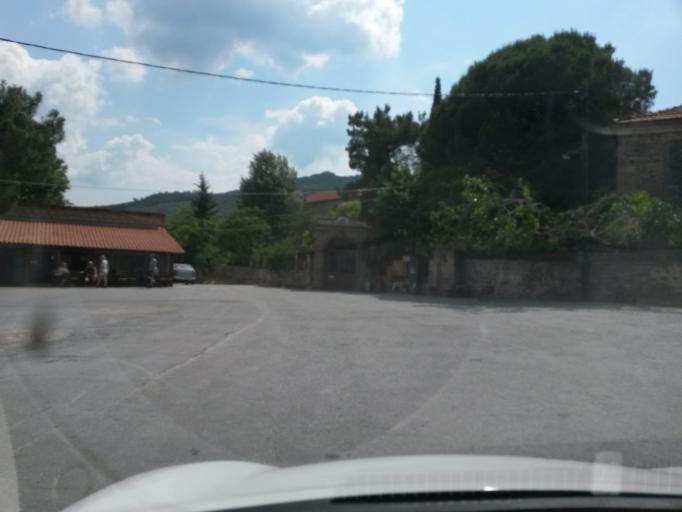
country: GR
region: North Aegean
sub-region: Nomos Lesvou
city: Kalloni
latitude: 39.2483
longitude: 26.1733
